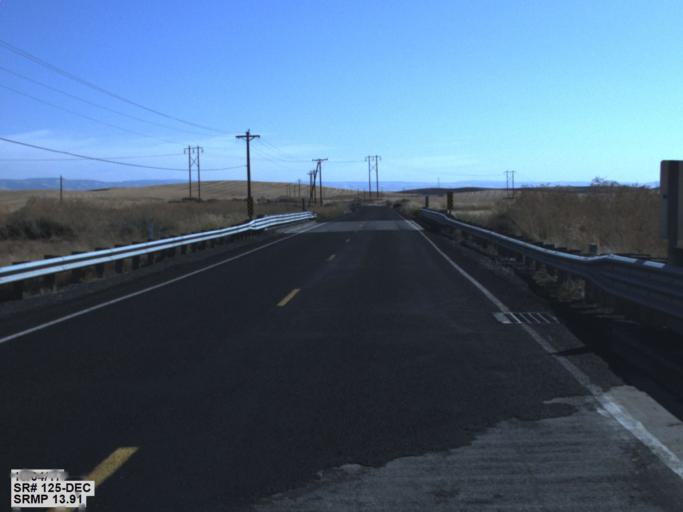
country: US
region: Washington
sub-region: Walla Walla County
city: Walla Walla
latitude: 46.1703
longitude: -118.3833
